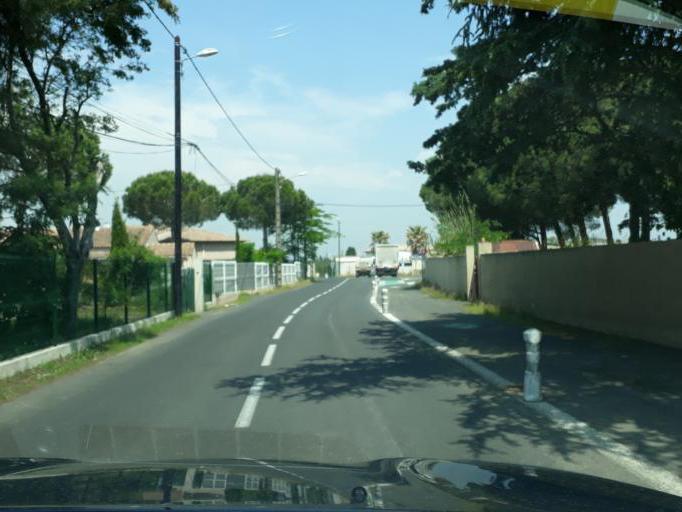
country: FR
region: Languedoc-Roussillon
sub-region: Departement de l'Herault
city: Agde
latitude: 43.2900
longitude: 3.4634
